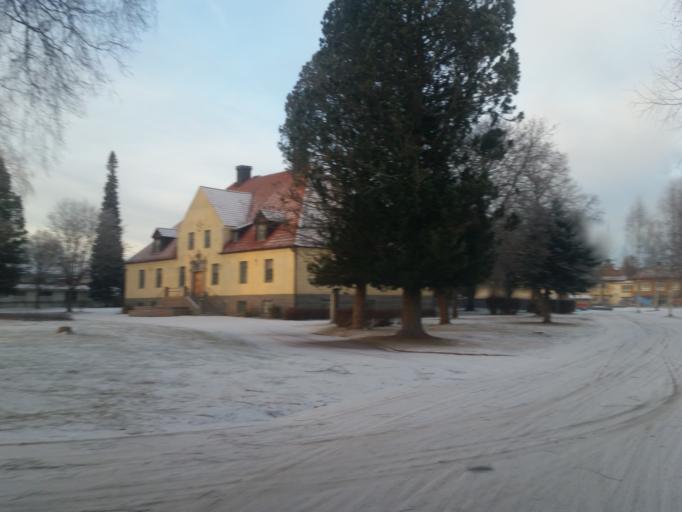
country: SE
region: Dalarna
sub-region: Leksand Municipality
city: Leksand
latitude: 60.7316
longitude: 14.9902
